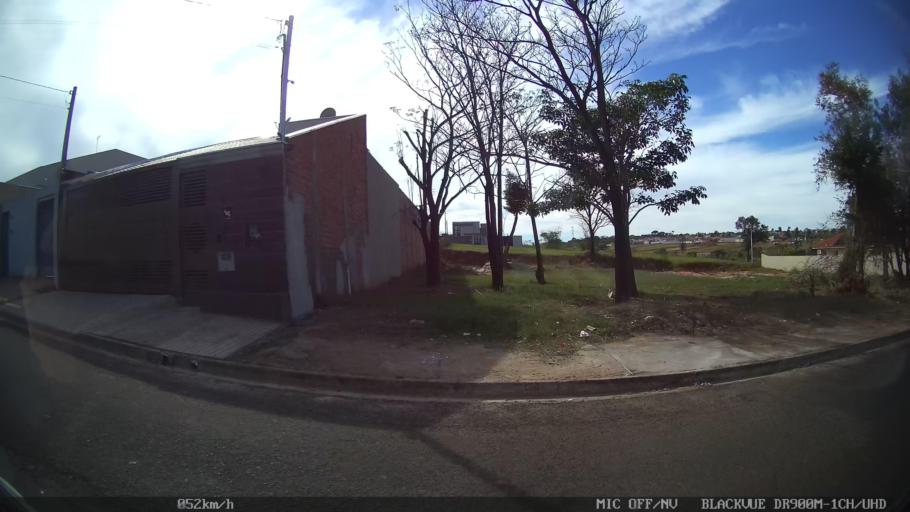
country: BR
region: Sao Paulo
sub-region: Catanduva
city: Catanduva
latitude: -21.1193
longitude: -48.9603
